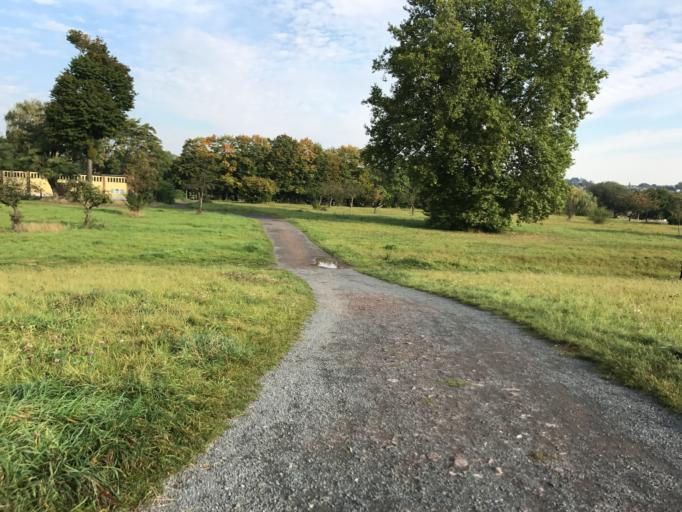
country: DE
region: Saxony
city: Albertstadt
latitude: 51.0610
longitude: 13.7716
